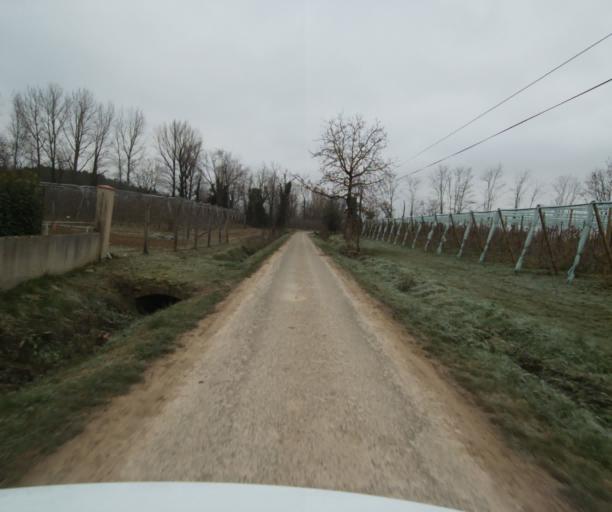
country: FR
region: Midi-Pyrenees
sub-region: Departement du Tarn-et-Garonne
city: Moissac
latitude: 44.1170
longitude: 1.1461
